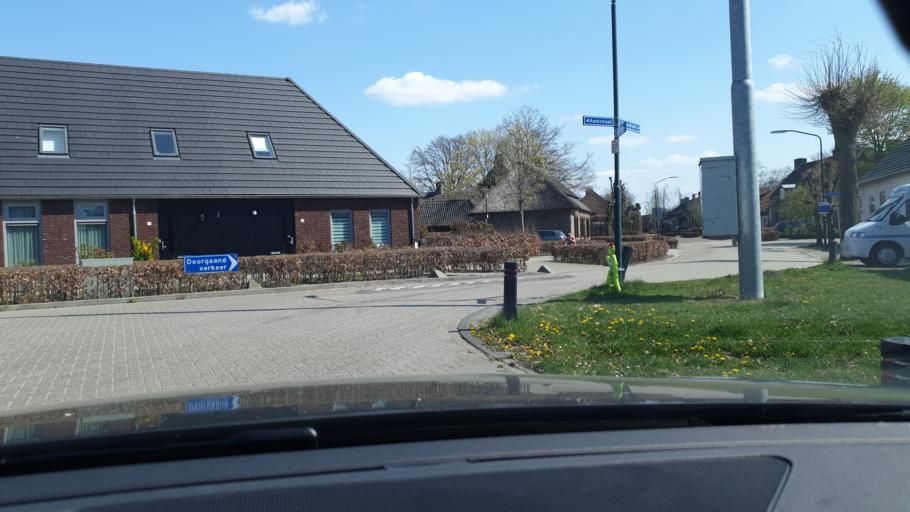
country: NL
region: North Brabant
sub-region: Gemeente Bladel en Netersel
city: Bladel
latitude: 51.3954
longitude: 5.2382
